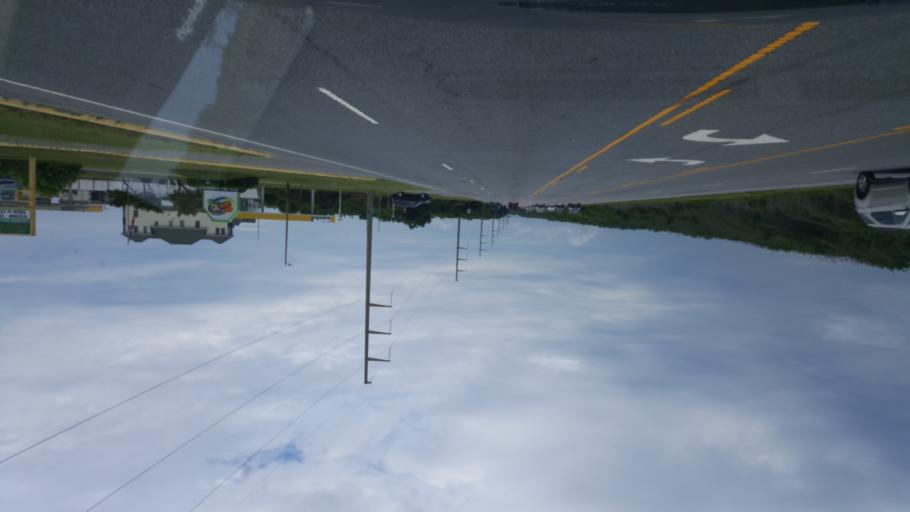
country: US
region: North Carolina
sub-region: Dare County
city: Nags Head
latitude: 35.9640
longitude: -75.6286
